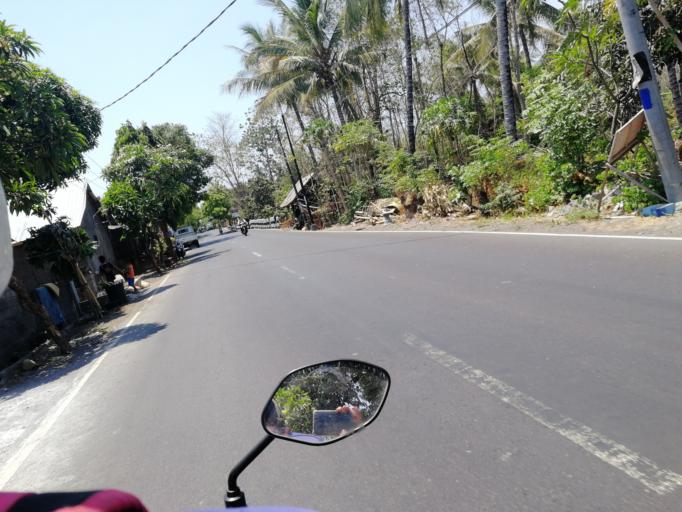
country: ID
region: Bali
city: Banjar Trunyan
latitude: -8.1514
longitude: 115.4124
